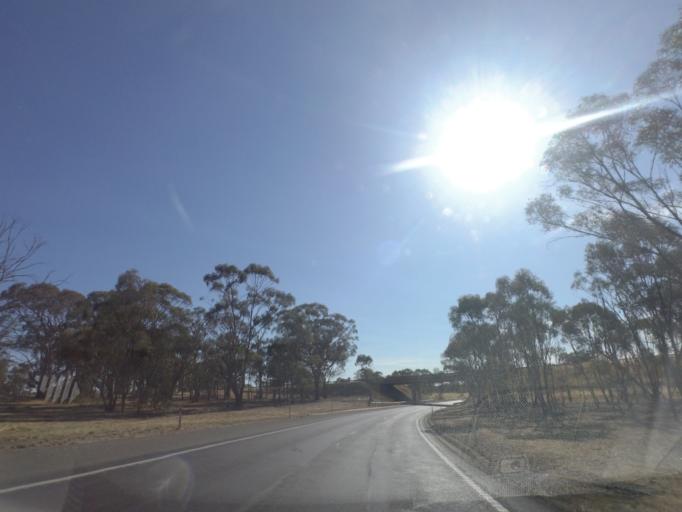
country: AU
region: Victoria
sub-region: Murrindindi
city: Kinglake West
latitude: -36.9851
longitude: 145.1444
